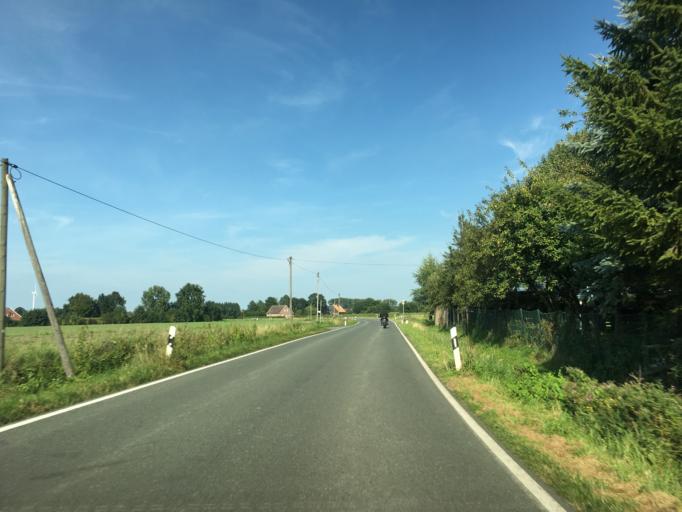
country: DE
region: North Rhine-Westphalia
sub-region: Regierungsbezirk Munster
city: Havixbeck
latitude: 52.0097
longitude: 7.4369
